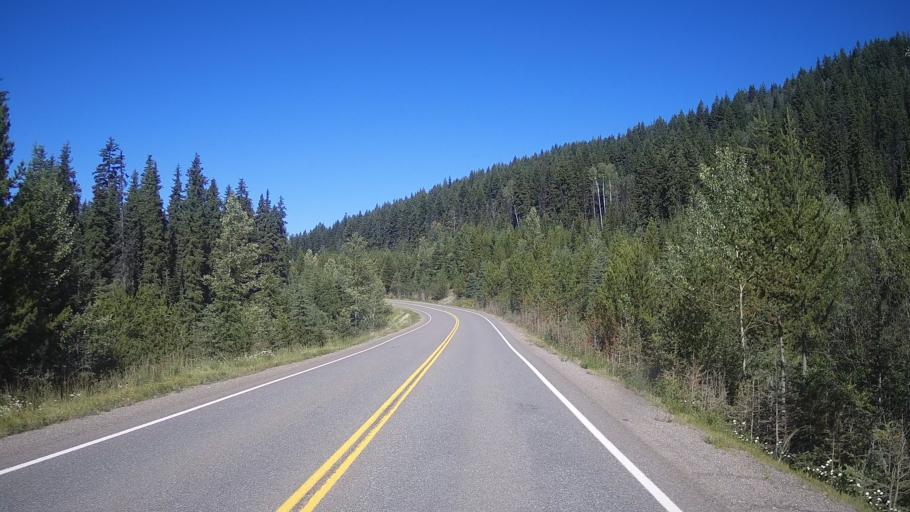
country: CA
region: British Columbia
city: Kamloops
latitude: 51.4962
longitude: -120.4182
